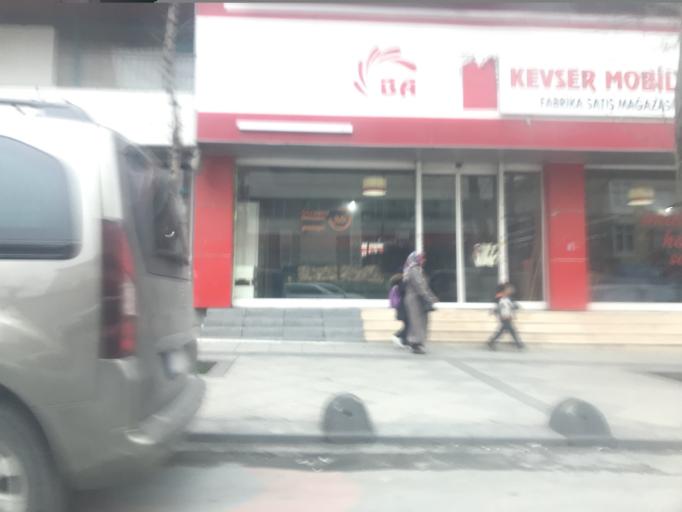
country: TR
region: Istanbul
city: Bagcilar
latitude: 41.0294
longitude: 28.8352
